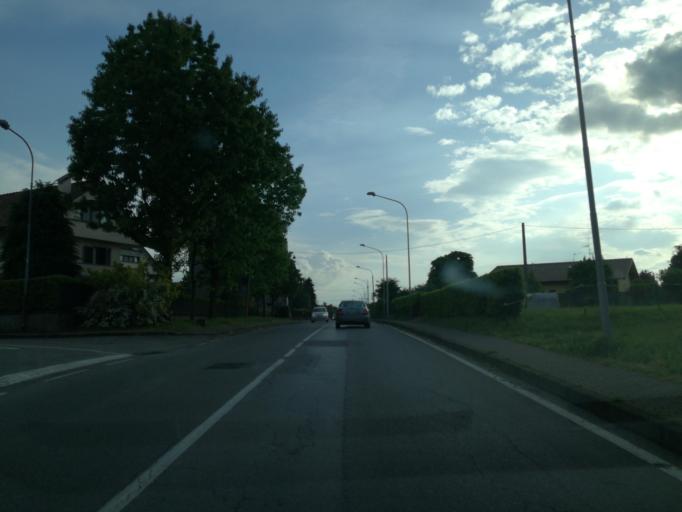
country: IT
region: Lombardy
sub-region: Provincia di Lecco
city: Paderno d'Adda
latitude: 45.6770
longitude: 9.4489
